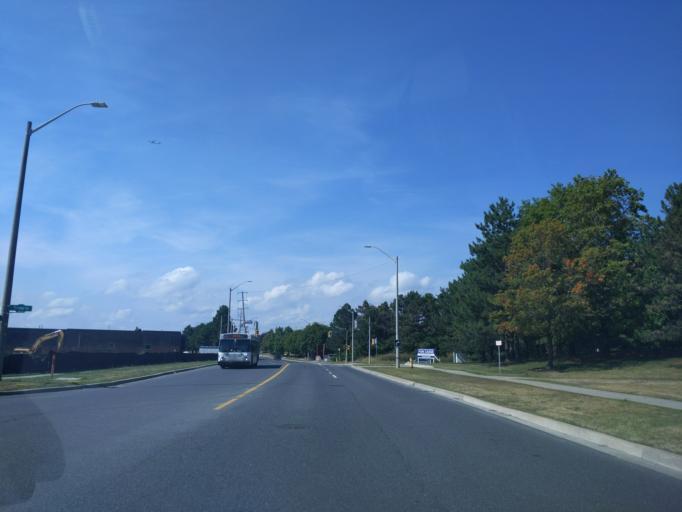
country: CA
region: Ontario
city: Willowdale
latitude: 43.8177
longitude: -79.3422
